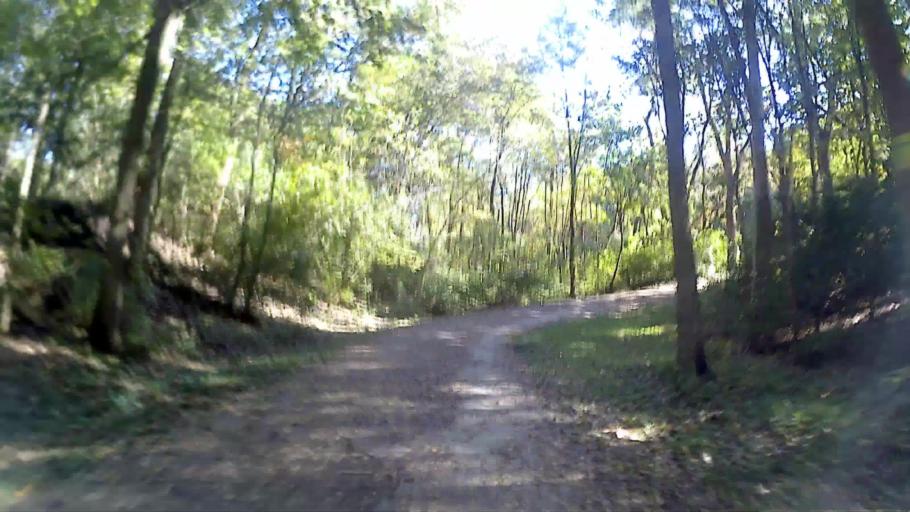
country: US
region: Illinois
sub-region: DuPage County
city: Glen Ellyn
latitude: 41.8808
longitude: -88.0417
